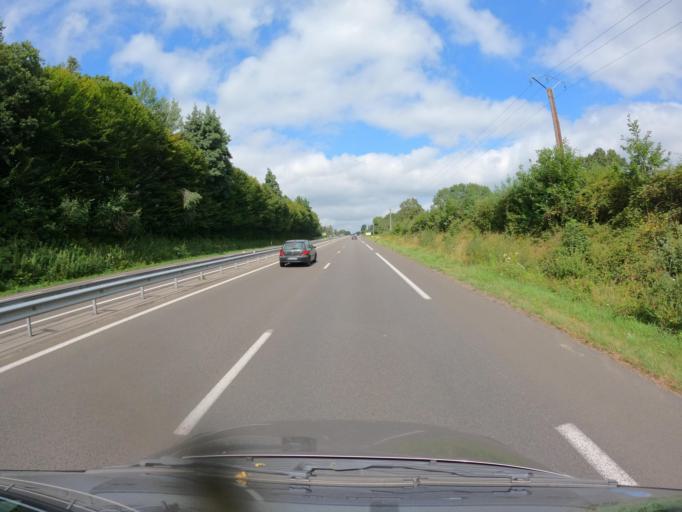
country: FR
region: Limousin
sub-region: Departement de la Haute-Vienne
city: Isle
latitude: 45.8416
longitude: 1.1809
